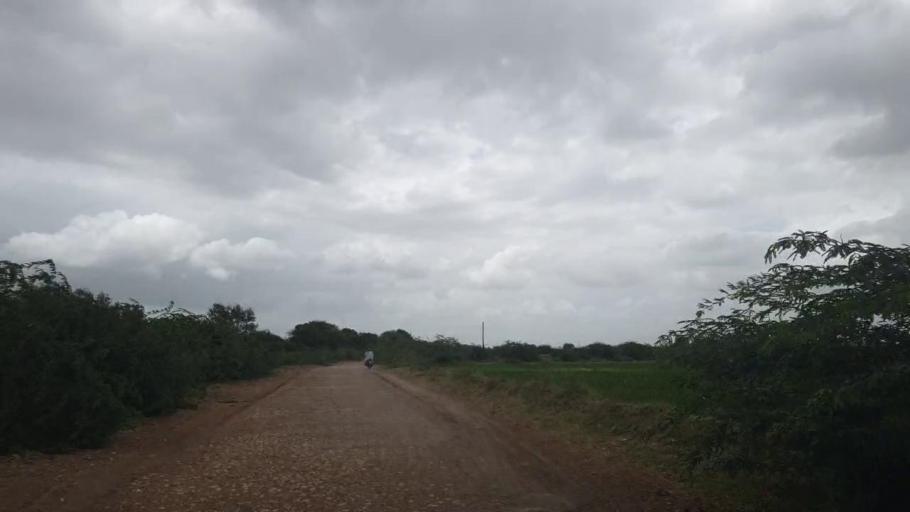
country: PK
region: Sindh
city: Badin
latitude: 24.6578
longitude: 68.9478
